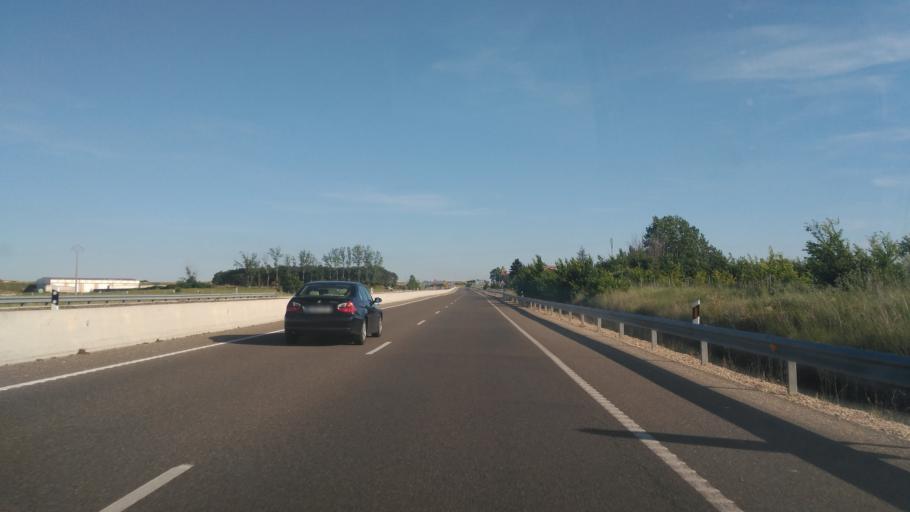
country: ES
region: Castille and Leon
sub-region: Provincia de Zamora
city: Zamora
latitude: 41.4771
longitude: -5.7404
